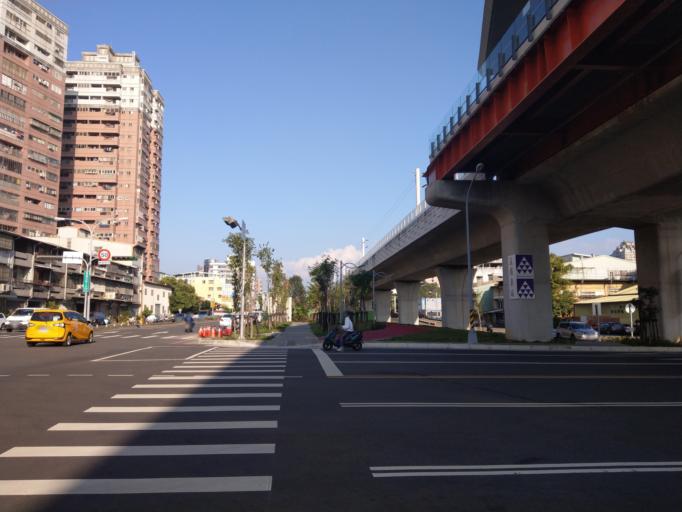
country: TW
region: Taiwan
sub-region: Taichung City
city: Taichung
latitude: 24.1292
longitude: 120.6669
